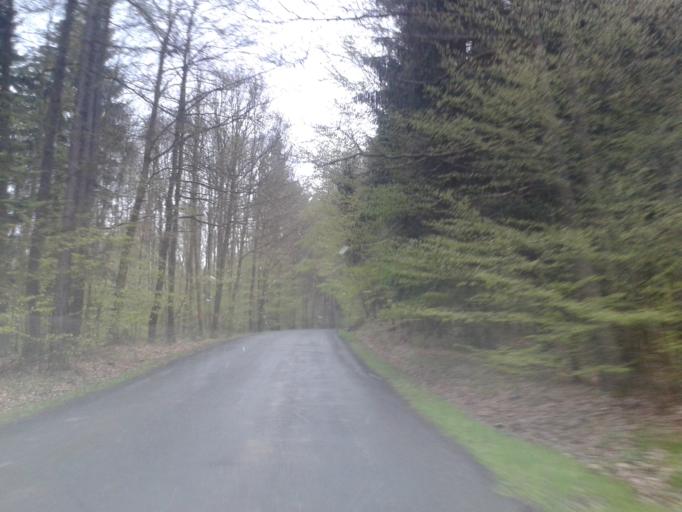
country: CZ
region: Central Bohemia
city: Hudlice
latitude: 49.9555
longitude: 13.9281
